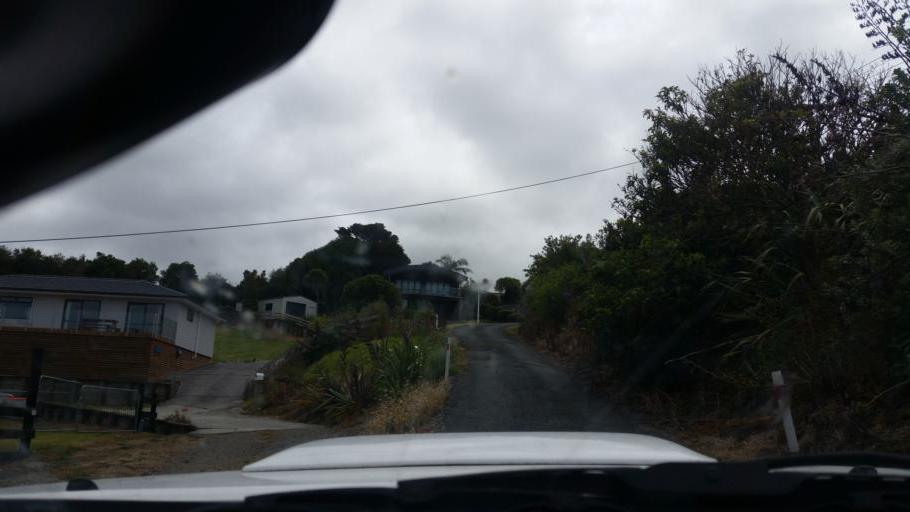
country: NZ
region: Auckland
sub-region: Auckland
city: Wellsford
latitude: -36.1566
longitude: 174.2363
